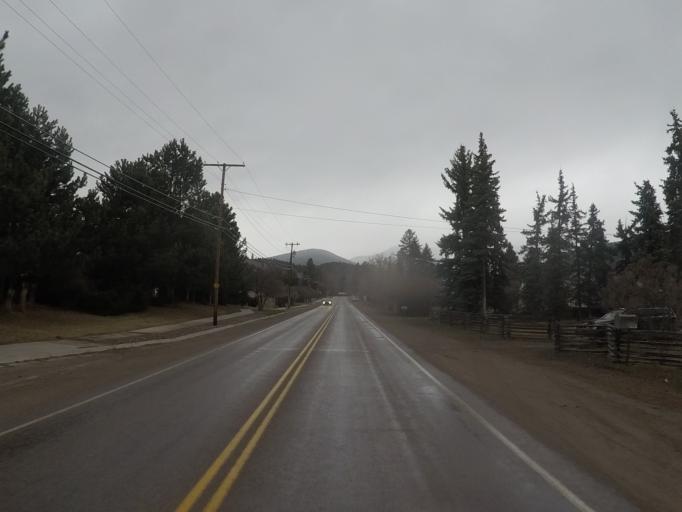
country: US
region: Montana
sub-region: Missoula County
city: East Missoula
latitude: 46.8965
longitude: -113.9656
